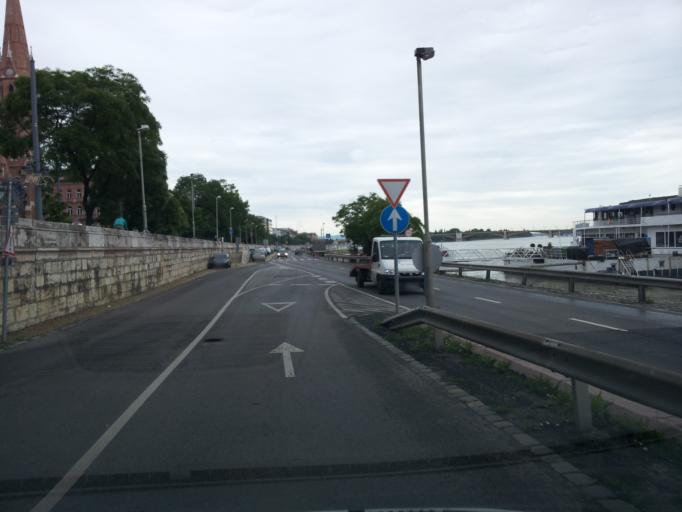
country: HU
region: Budapest
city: Budapest
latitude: 47.5029
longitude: 19.0400
